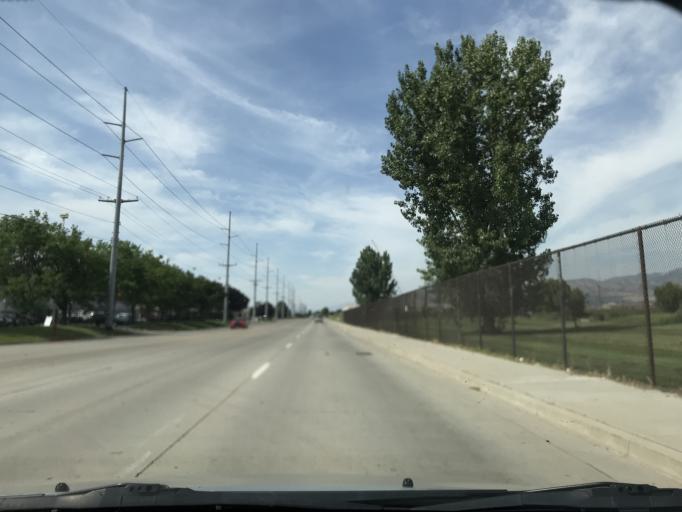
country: US
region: Utah
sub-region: Salt Lake County
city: Centerfield
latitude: 40.7038
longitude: -111.9169
